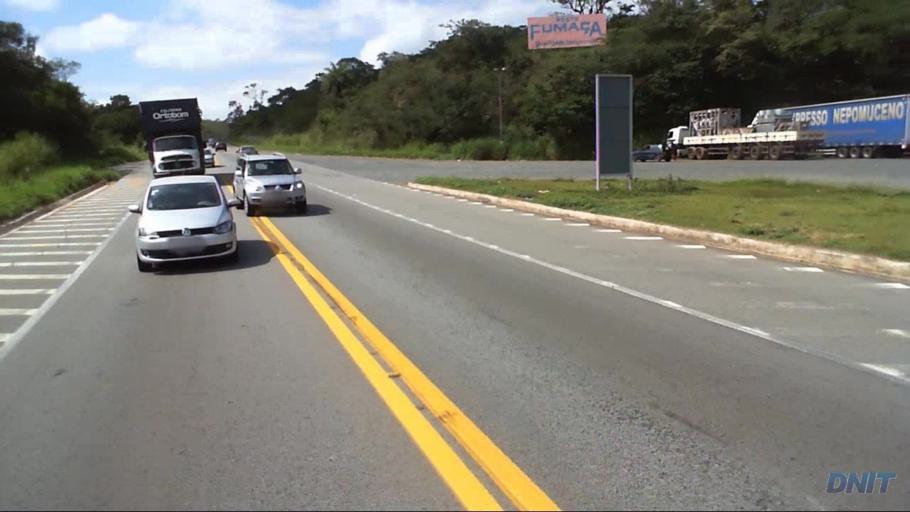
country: BR
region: Minas Gerais
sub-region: Santa Luzia
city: Santa Luzia
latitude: -19.8126
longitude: -43.7975
